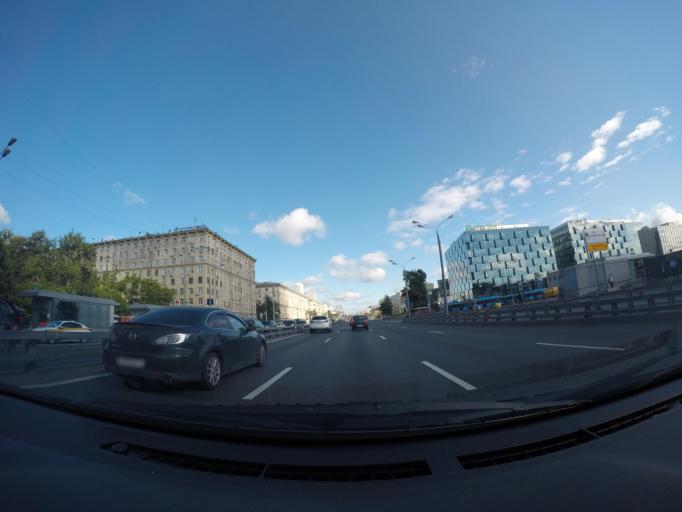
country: RU
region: Moskovskaya
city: Koptevo
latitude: 55.8196
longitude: 37.4975
